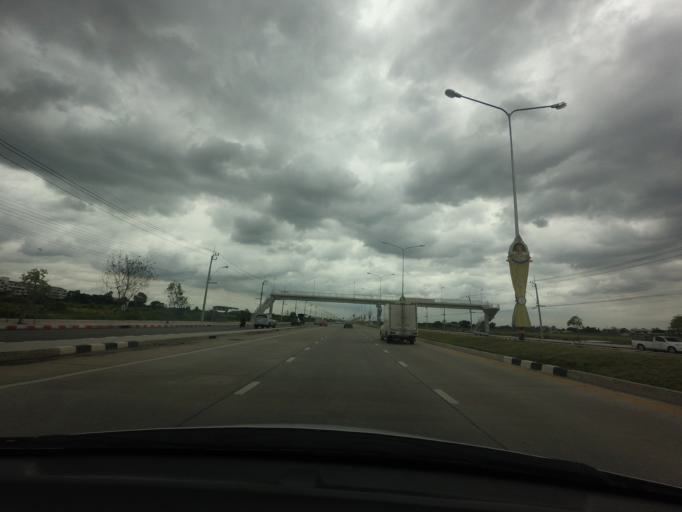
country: TH
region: Bangkok
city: Saphan Sung
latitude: 13.7551
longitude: 100.7286
